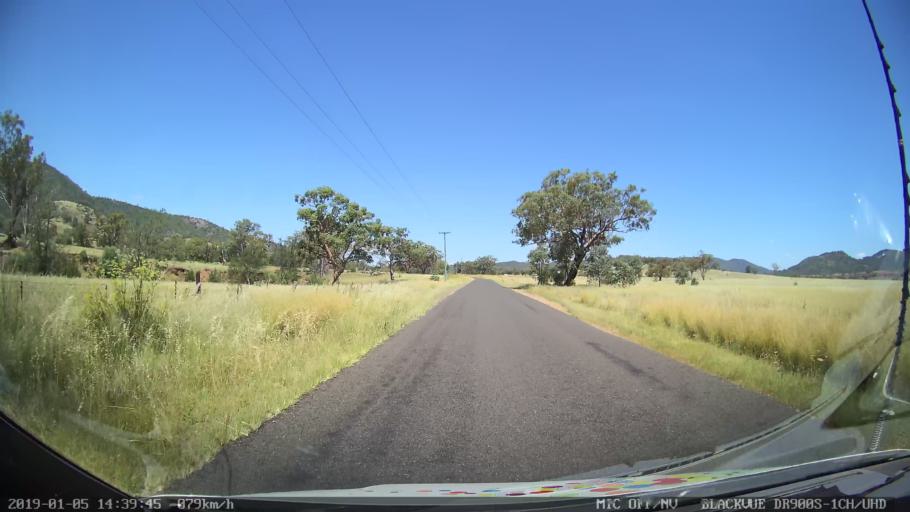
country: AU
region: New South Wales
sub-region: Tamworth Municipality
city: Phillip
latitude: -31.2557
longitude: 150.7043
